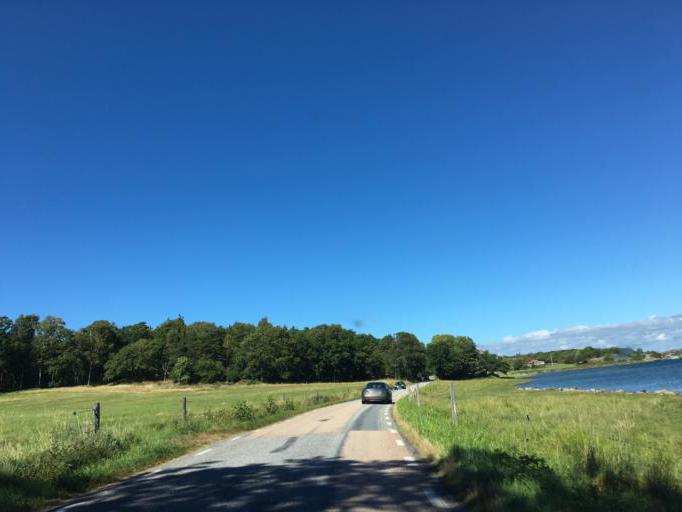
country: SE
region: Vaestra Goetaland
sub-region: Sotenas Kommun
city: Hunnebostrand
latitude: 58.4210
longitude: 11.2653
